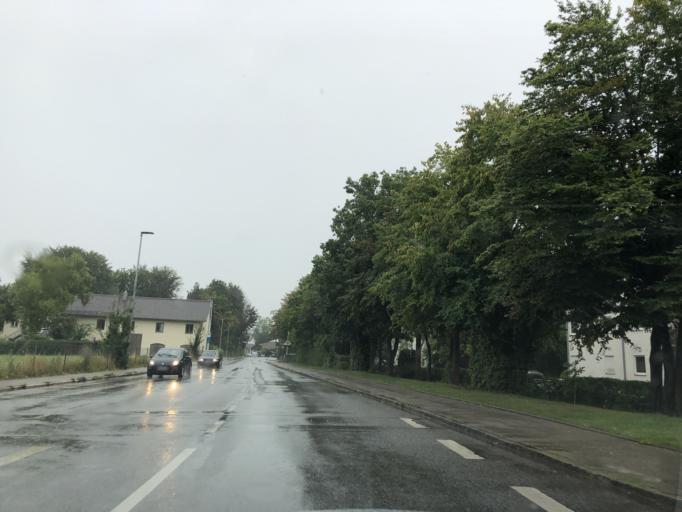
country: DE
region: Bavaria
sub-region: Upper Bavaria
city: Erding
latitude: 48.3027
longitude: 11.8970
